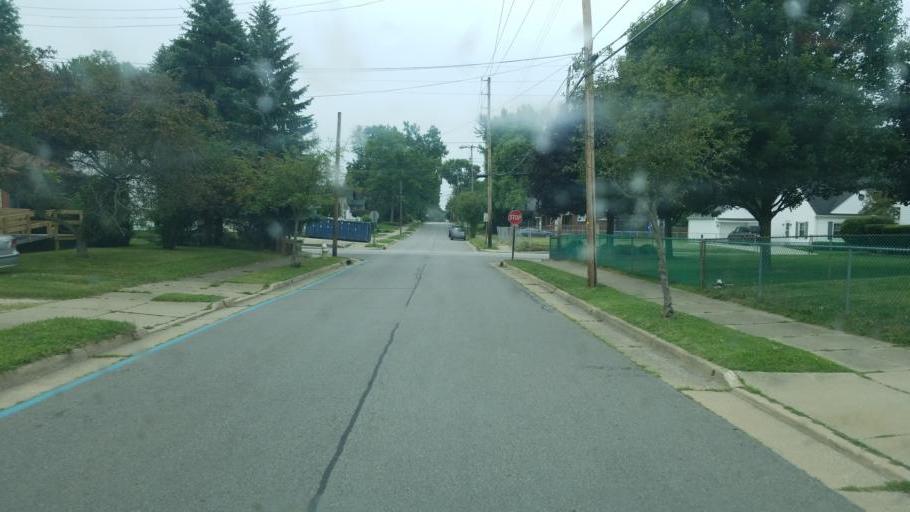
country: US
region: Ohio
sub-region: Summit County
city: Sawyerwood
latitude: 41.0499
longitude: -81.4261
